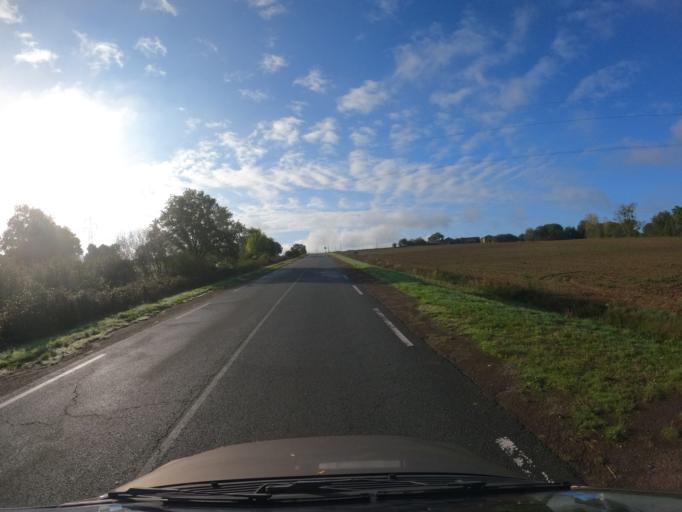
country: FR
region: Pays de la Loire
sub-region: Departement de Maine-et-Loire
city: La Seguiniere
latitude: 47.0586
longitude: -0.9455
